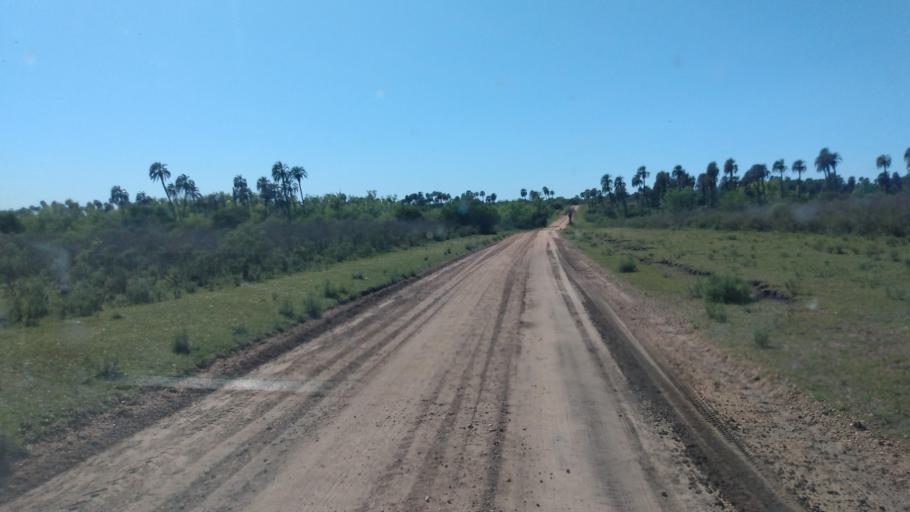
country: AR
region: Entre Rios
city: Ubajay
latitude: -31.8680
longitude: -58.2484
